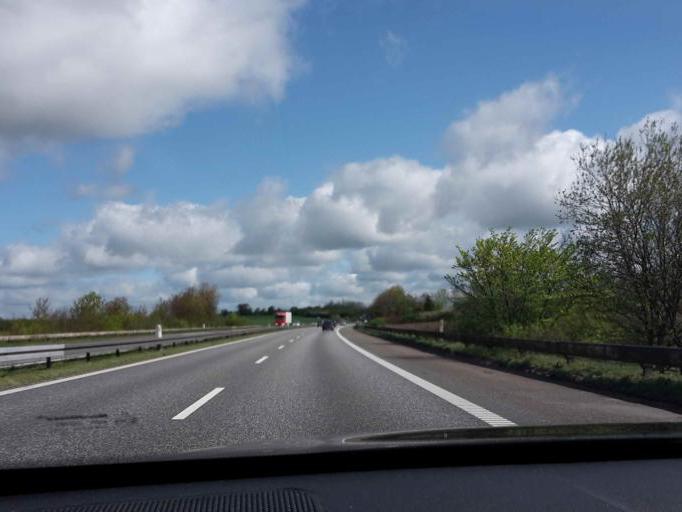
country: DK
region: Central Jutland
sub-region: Arhus Kommune
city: Framlev
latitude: 56.1344
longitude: 10.0357
